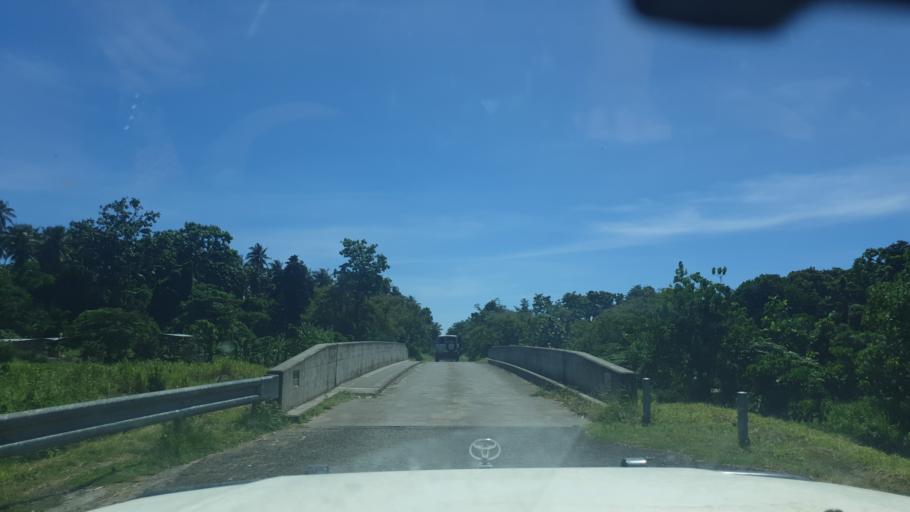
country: PG
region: Bougainville
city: Buka
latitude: -5.6603
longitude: 155.0966
